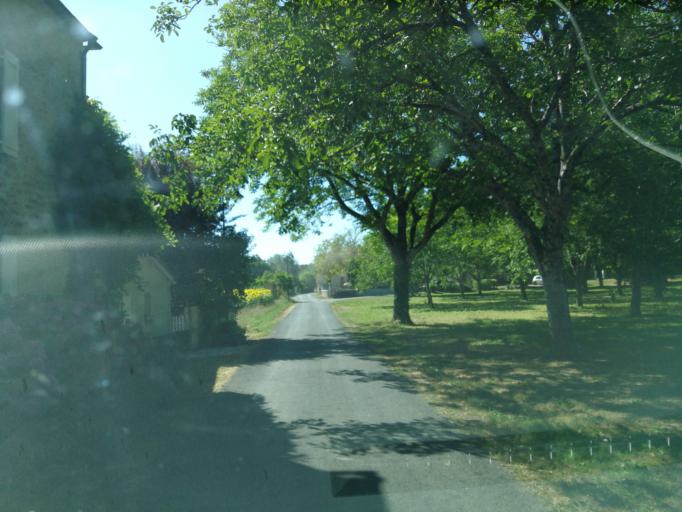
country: FR
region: Midi-Pyrenees
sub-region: Departement du Lot
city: Souillac
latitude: 44.8692
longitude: 1.4369
